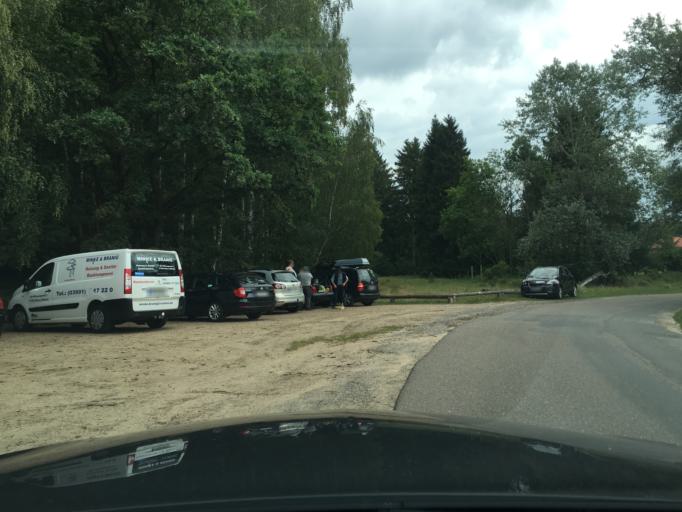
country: DE
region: Mecklenburg-Vorpommern
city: Mollenhagen
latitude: 53.4410
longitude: 12.8386
